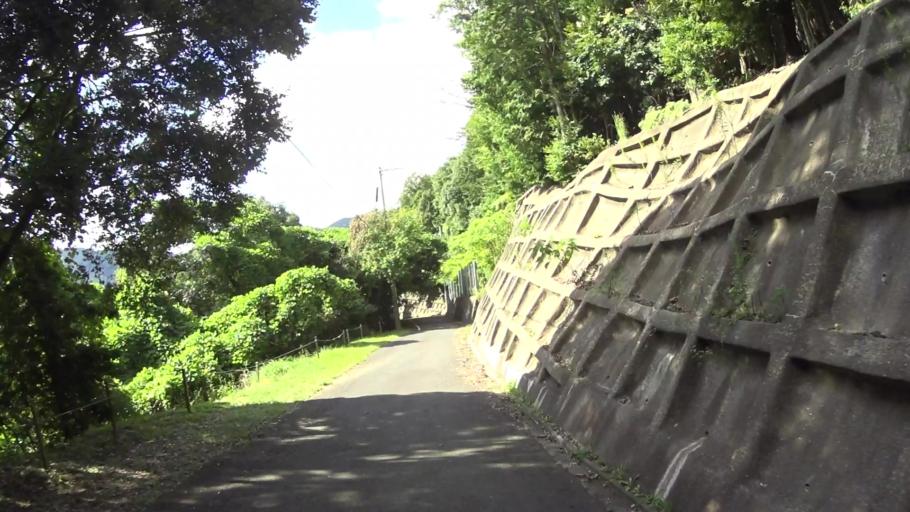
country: JP
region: Shiga Prefecture
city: Otsu-shi
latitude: 34.9406
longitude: 135.8625
